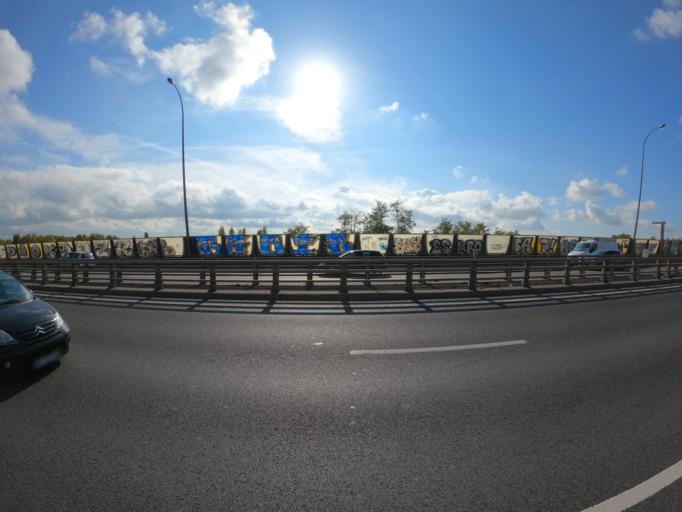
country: FR
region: Ile-de-France
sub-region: Departement du Val-de-Marne
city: Choisy-le-Roi
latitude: 48.7764
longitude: 2.4197
